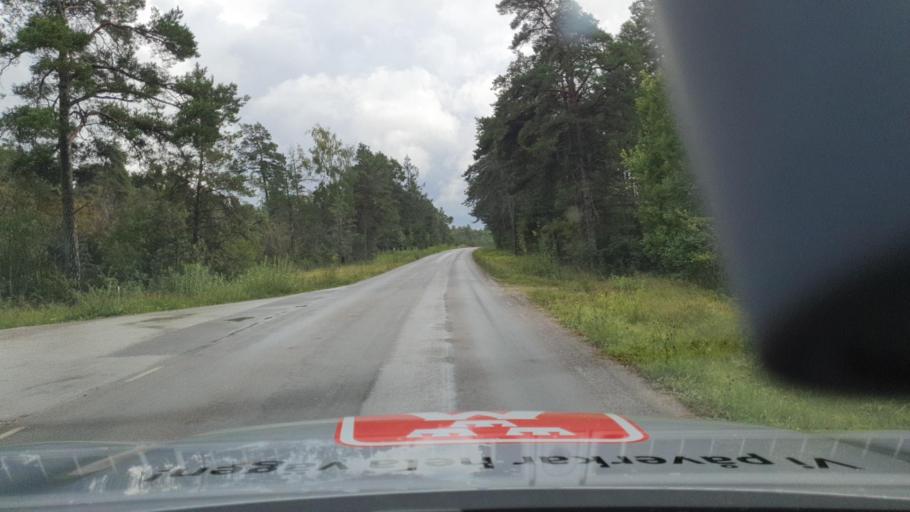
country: SE
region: Gotland
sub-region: Gotland
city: Slite
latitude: 57.7258
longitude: 18.7495
